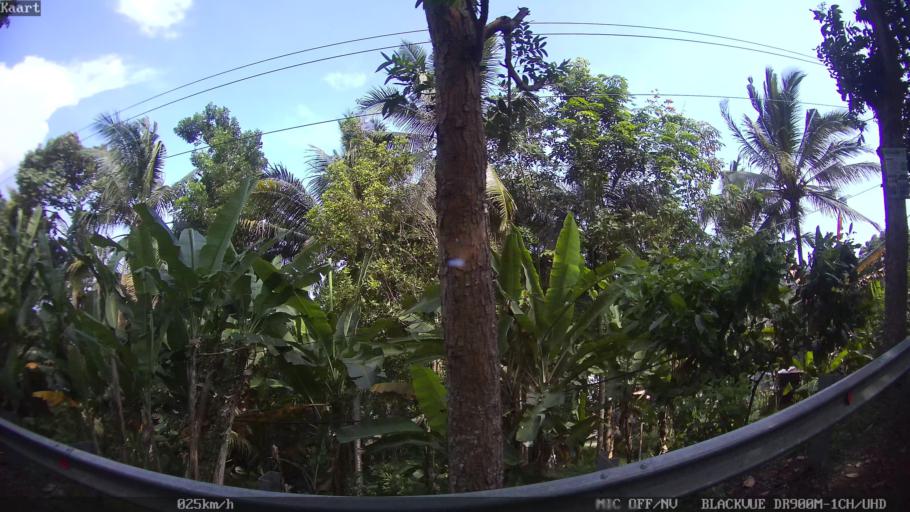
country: ID
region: Lampung
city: Bandarlampung
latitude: -5.4060
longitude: 105.2296
